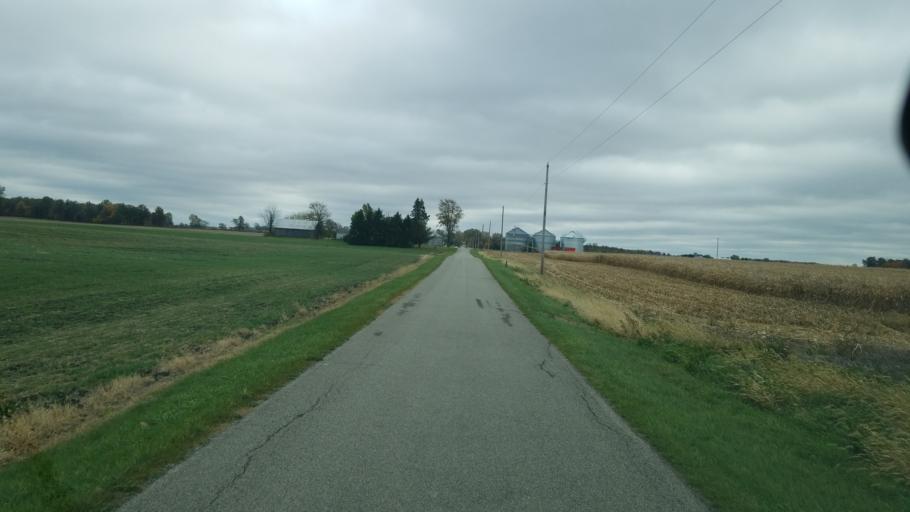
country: US
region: Ohio
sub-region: Crawford County
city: Bucyrus
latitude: 40.9071
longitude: -82.8779
